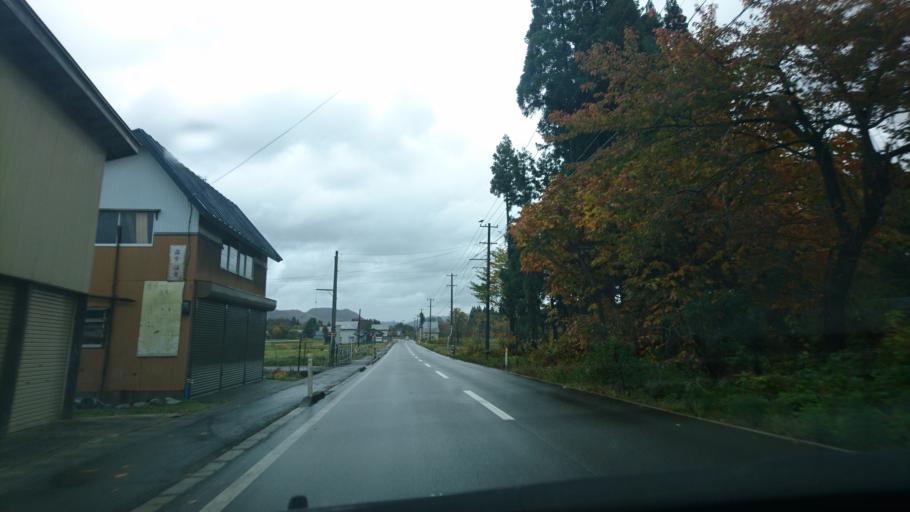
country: JP
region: Akita
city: Kakunodatemachi
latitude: 39.4548
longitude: 140.7691
